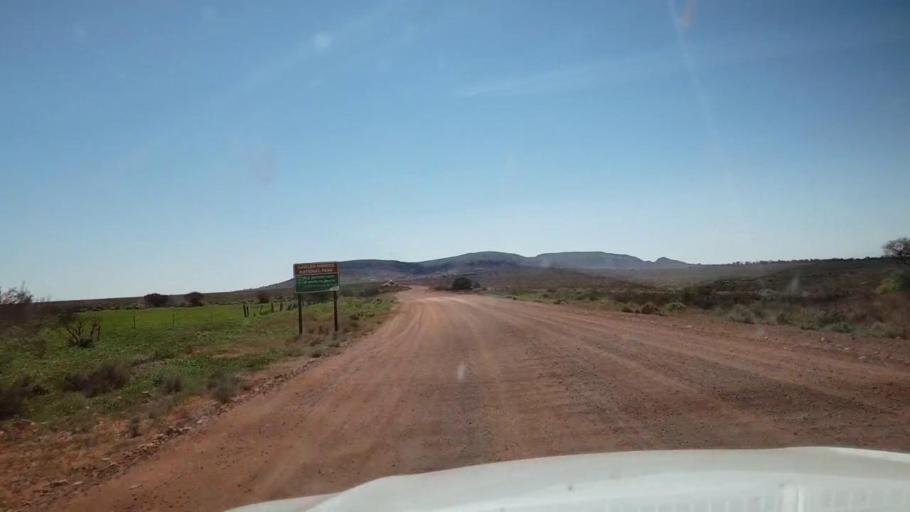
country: AU
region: South Australia
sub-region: Whyalla
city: Whyalla
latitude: -32.7157
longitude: 137.1431
